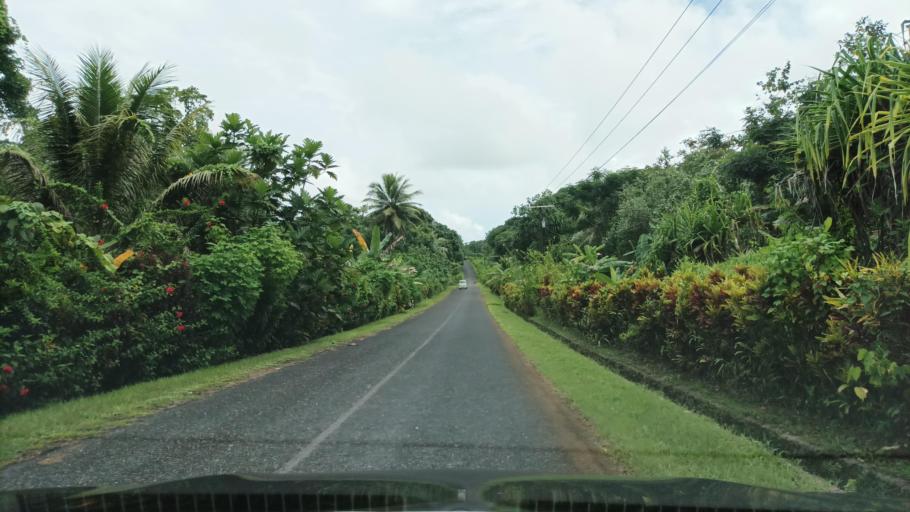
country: FM
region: Pohnpei
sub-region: Madolenihm Municipality
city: Madolenihm Municipality Government
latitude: 6.8231
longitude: 158.2975
